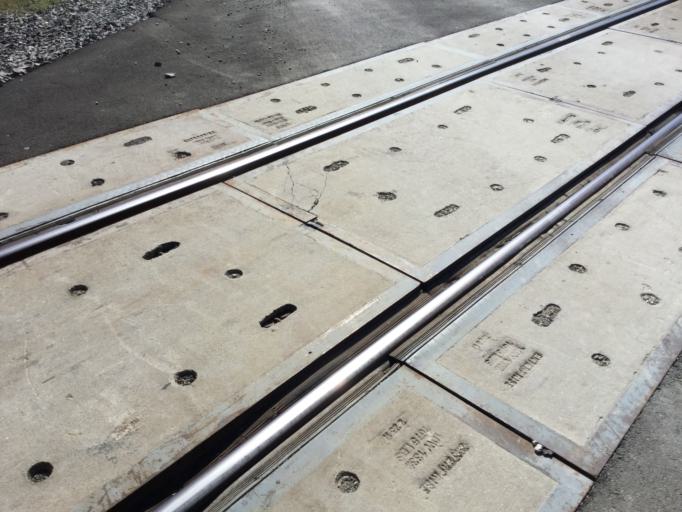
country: US
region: Kansas
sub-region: Labette County
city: Oswego
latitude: 37.2079
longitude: -95.1600
